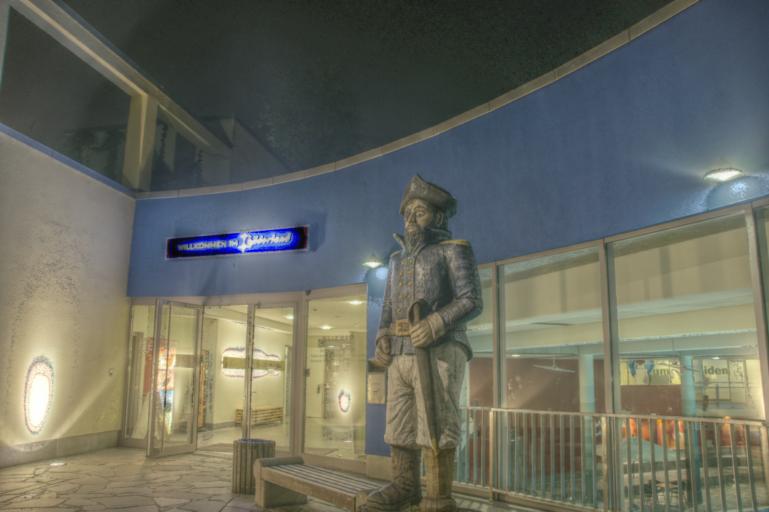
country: DE
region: Hamburg
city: Bergedorf
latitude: 53.4925
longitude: 10.2130
